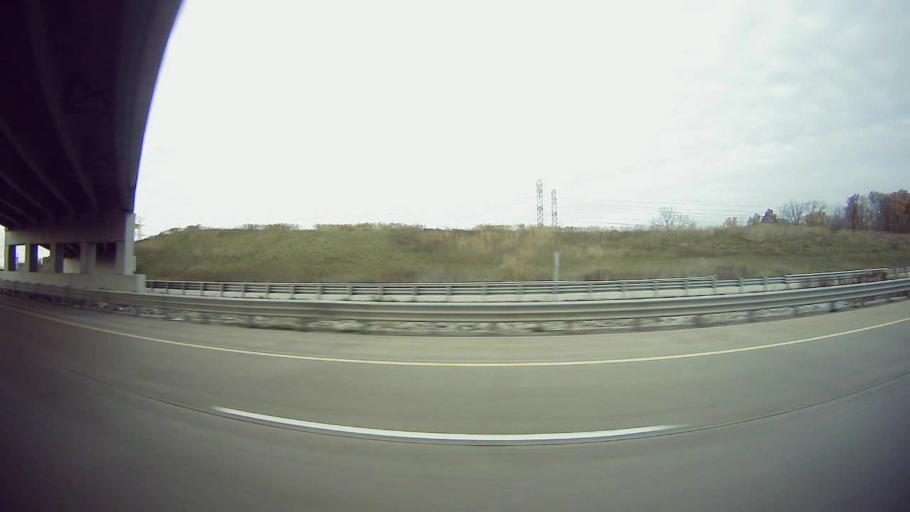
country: US
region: Michigan
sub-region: Wayne County
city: Rockwood
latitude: 42.0852
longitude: -83.2417
